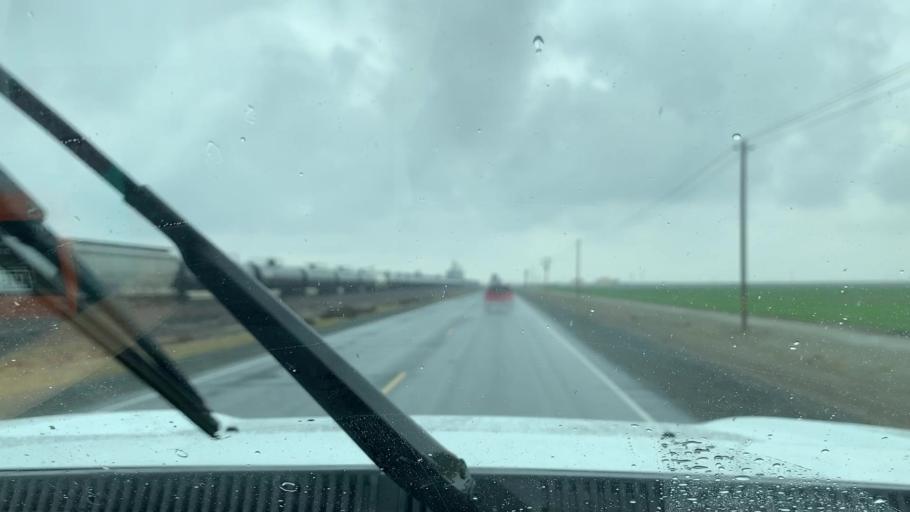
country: US
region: California
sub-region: Tulare County
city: Alpaugh
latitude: 35.9806
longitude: -119.4704
